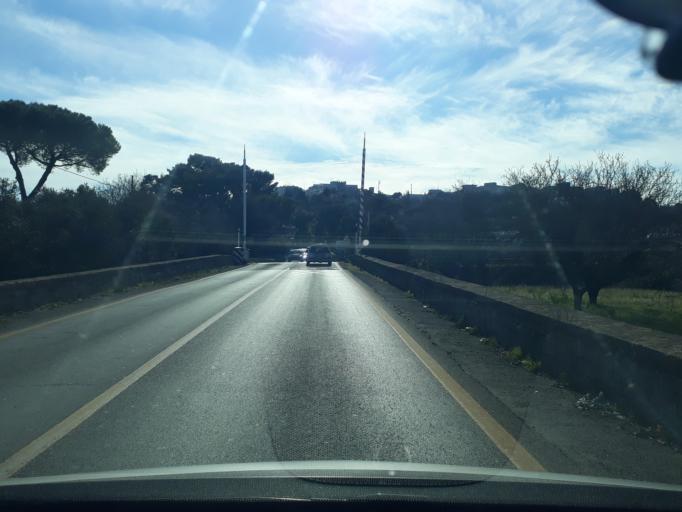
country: IT
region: Apulia
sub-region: Provincia di Taranto
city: Martina Franca
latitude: 40.7152
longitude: 17.3328
